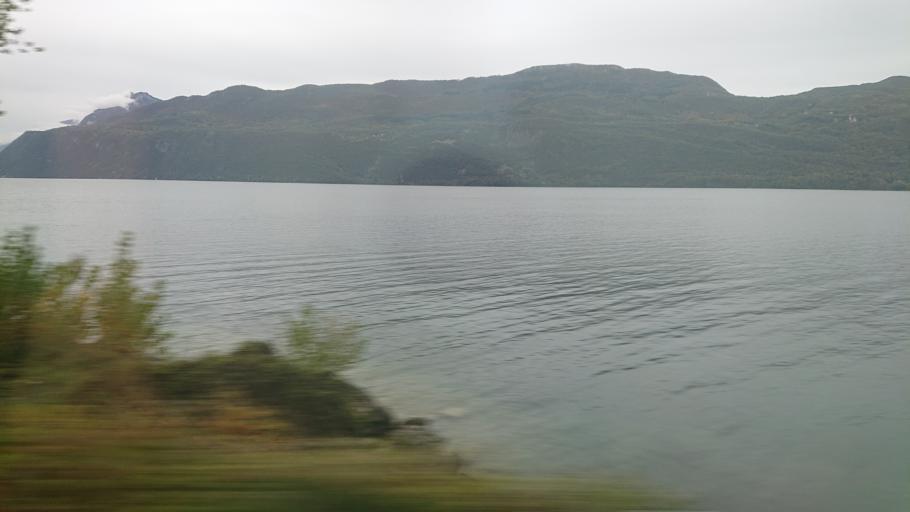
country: FR
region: Rhone-Alpes
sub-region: Departement de la Savoie
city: Brison-Saint-Innocent
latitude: 45.7543
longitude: 5.8789
